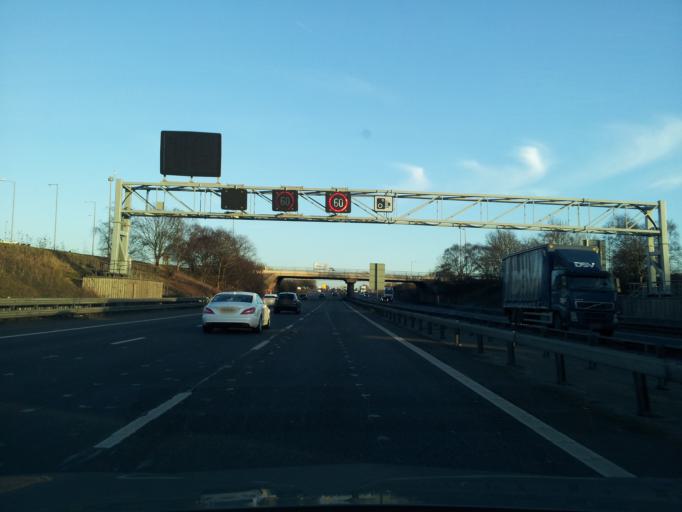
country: GB
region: England
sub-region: Central Bedfordshire
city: Husborne Crawley
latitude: 52.0271
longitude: -0.6053
